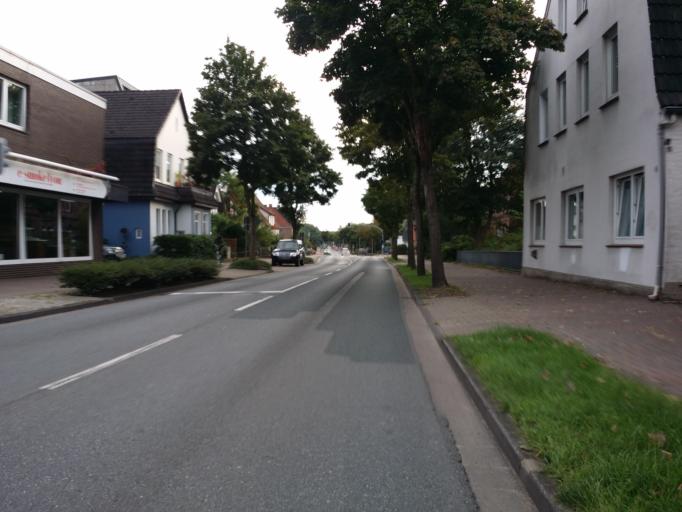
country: DE
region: Lower Saxony
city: Bremervorde
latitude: 53.4821
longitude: 9.1425
